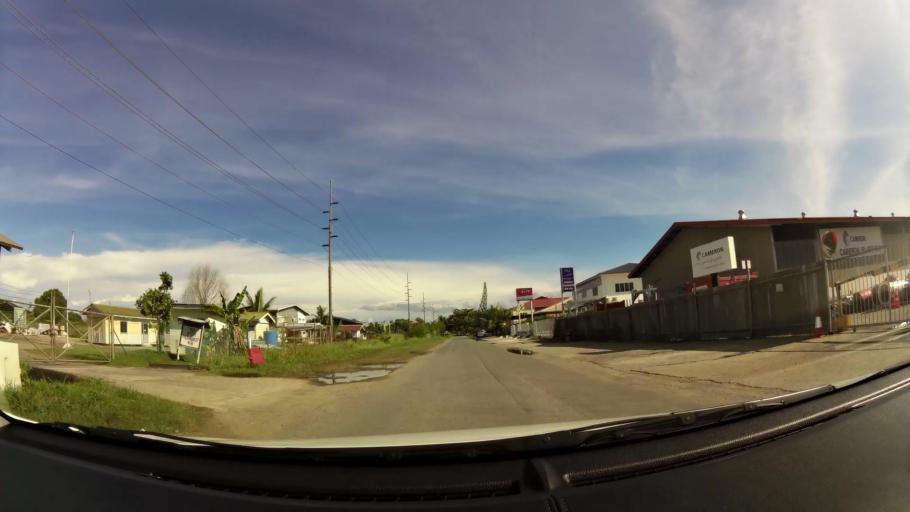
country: BN
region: Belait
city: Kuala Belait
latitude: 4.5735
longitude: 114.2091
